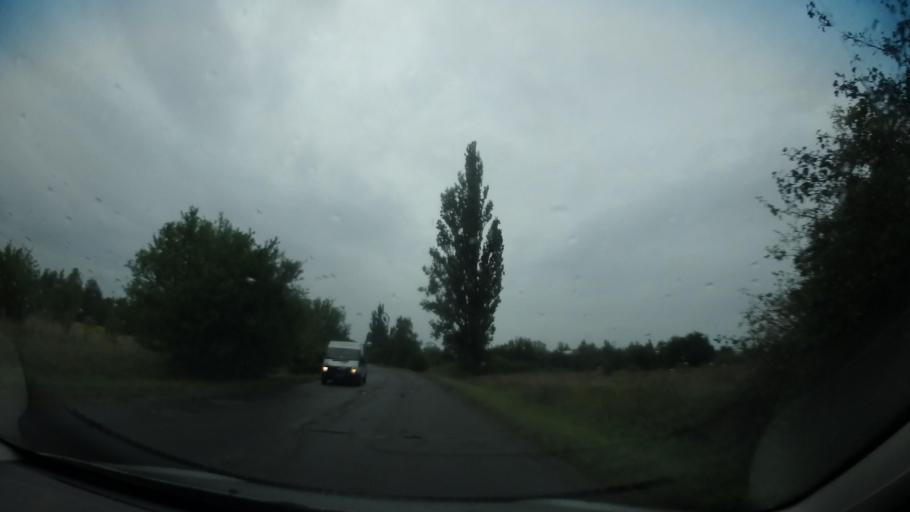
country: CZ
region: Central Bohemia
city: Milovice
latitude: 50.2357
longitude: 14.8970
